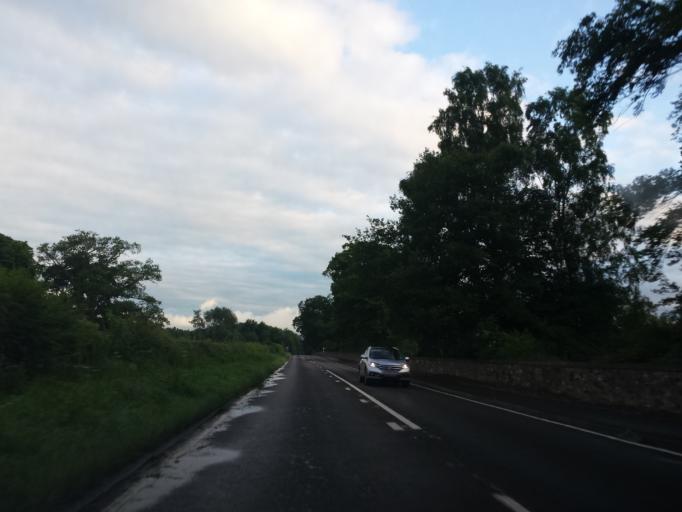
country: GB
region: Scotland
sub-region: Perth and Kinross
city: Perth
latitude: 56.4174
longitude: -3.4278
